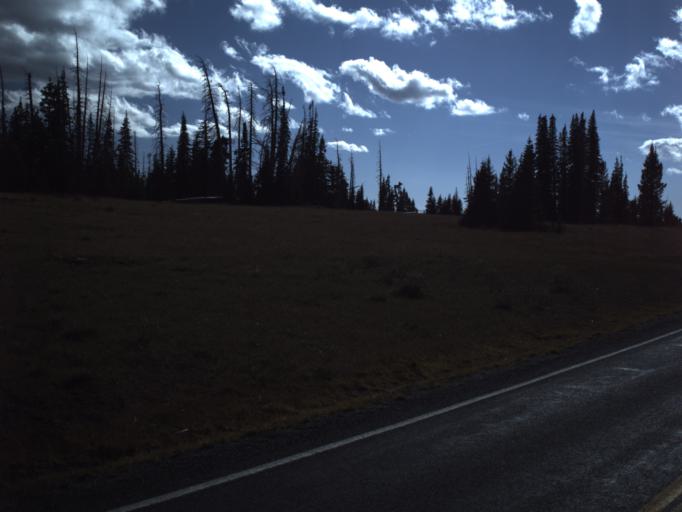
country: US
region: Utah
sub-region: Iron County
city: Parowan
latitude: 37.6553
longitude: -112.8242
